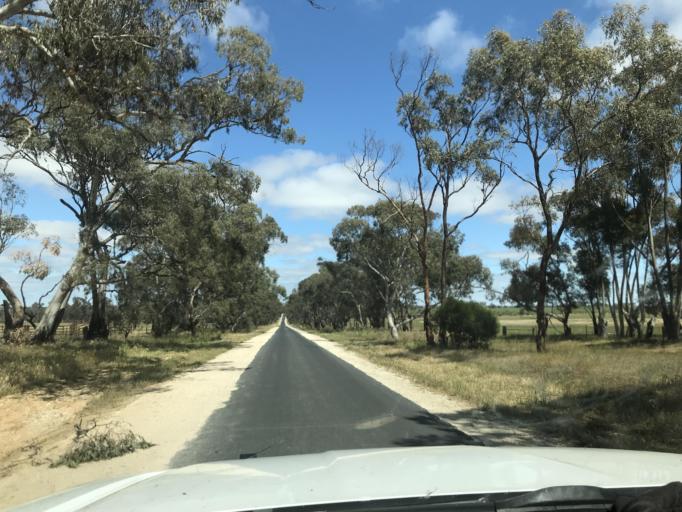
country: AU
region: South Australia
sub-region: Tatiara
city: Bordertown
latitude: -36.3062
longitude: 141.0727
